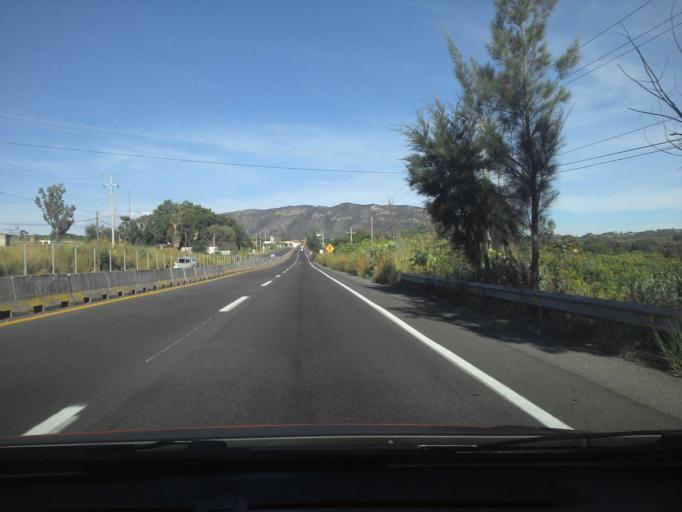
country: MX
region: Jalisco
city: La Venta del Astillero
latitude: 20.7289
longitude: -103.6125
